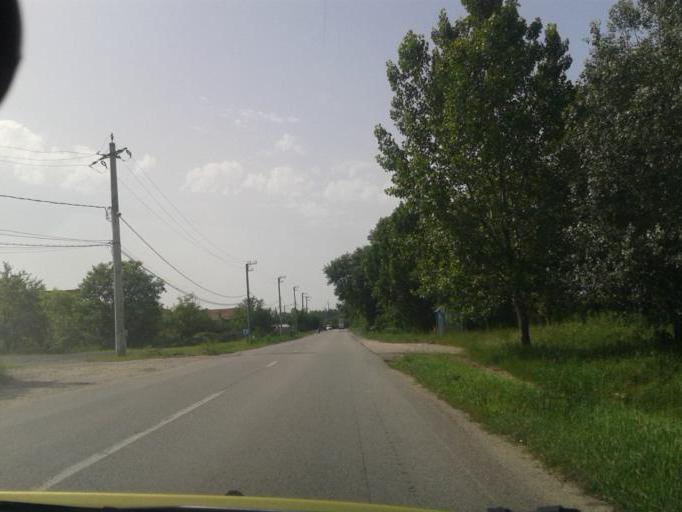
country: RO
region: Valcea
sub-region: Comuna Mihaesti
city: Mihaesti
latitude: 45.0485
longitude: 24.2518
